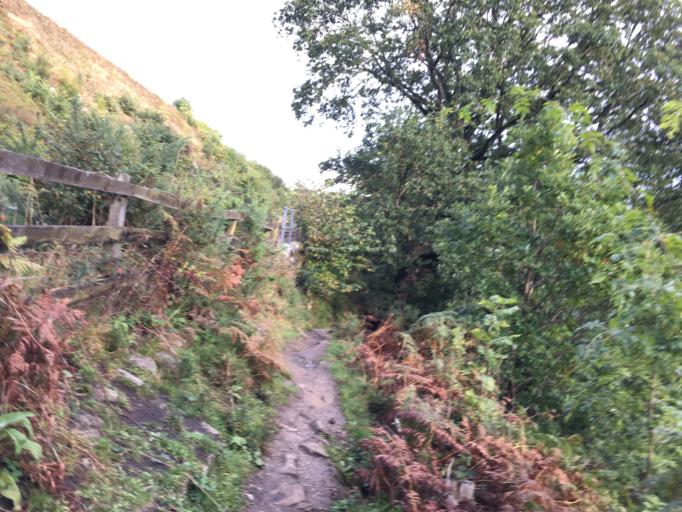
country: GB
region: England
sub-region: North Yorkshire
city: Sleights
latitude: 54.4095
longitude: -0.7338
